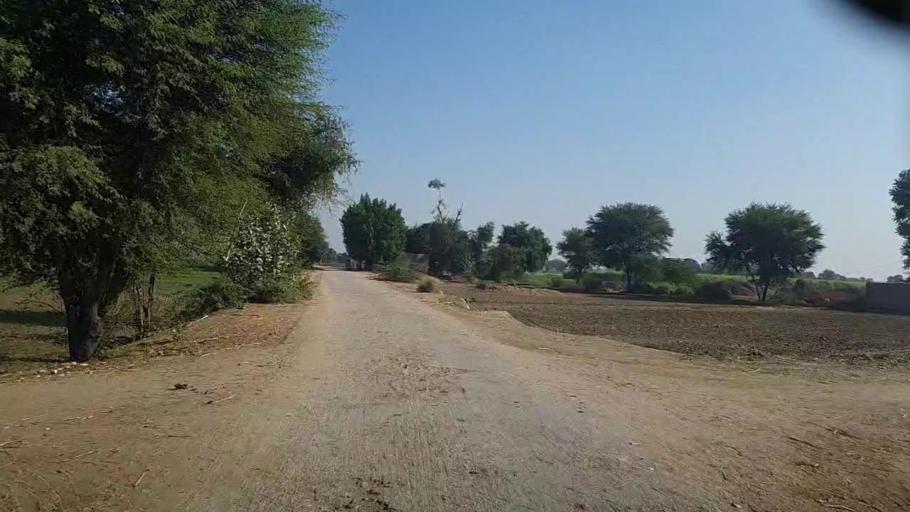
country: PK
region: Sindh
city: Darya Khan Marri
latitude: 26.6579
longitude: 68.3474
